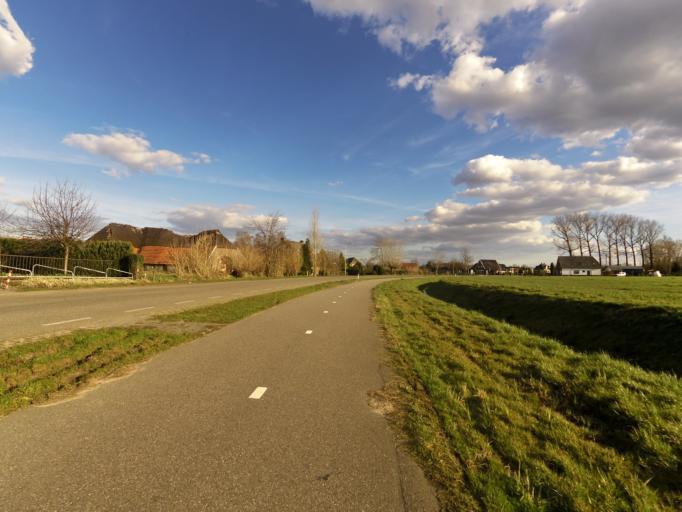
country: NL
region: Gelderland
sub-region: Gemeente Doesburg
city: Doesburg
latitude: 51.9569
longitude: 6.1381
